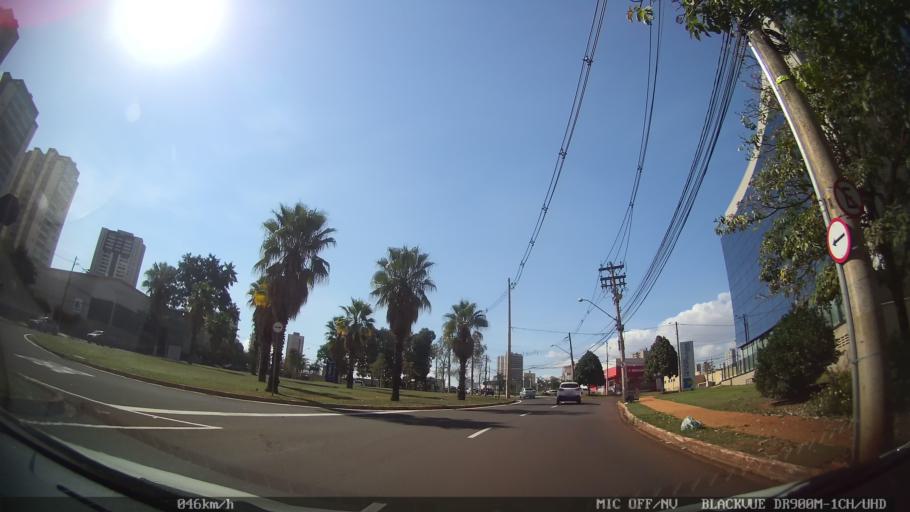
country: BR
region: Sao Paulo
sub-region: Ribeirao Preto
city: Ribeirao Preto
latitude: -21.2215
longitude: -47.8289
